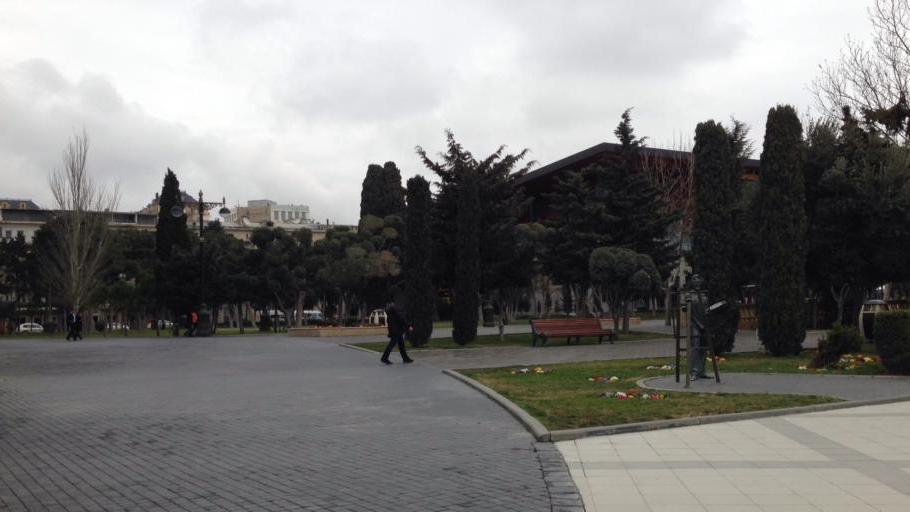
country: AZ
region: Baki
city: Baku
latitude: 40.3686
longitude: 49.8447
